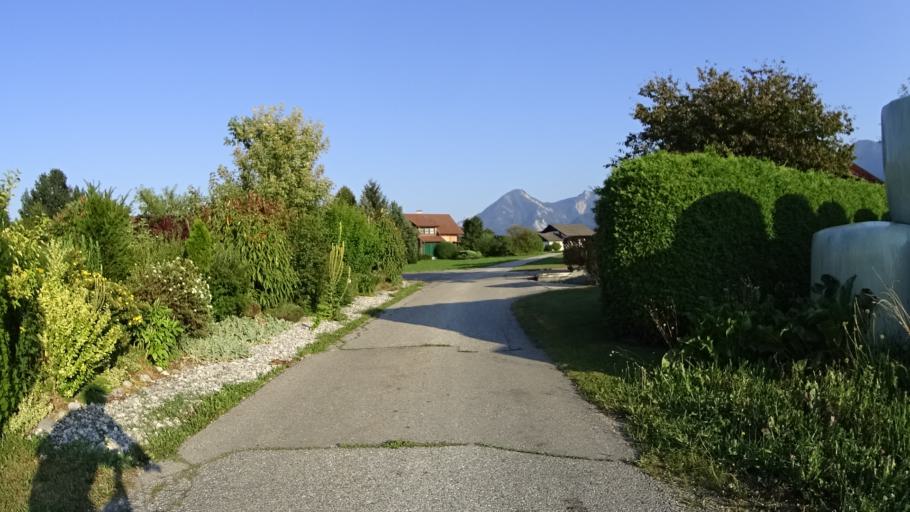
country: AT
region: Carinthia
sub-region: Politischer Bezirk Villach Land
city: Sankt Jakob
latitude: 46.5531
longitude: 14.0636
